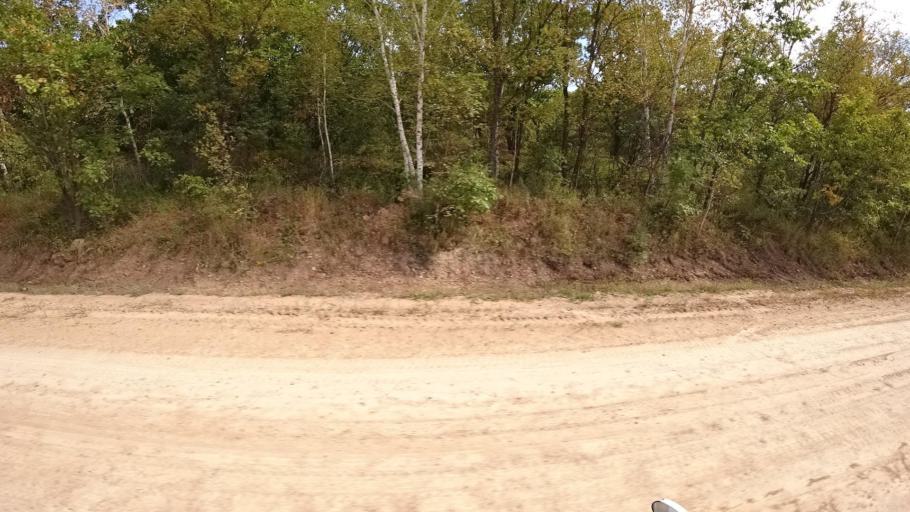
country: RU
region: Primorskiy
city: Yakovlevka
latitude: 44.7333
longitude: 133.6087
